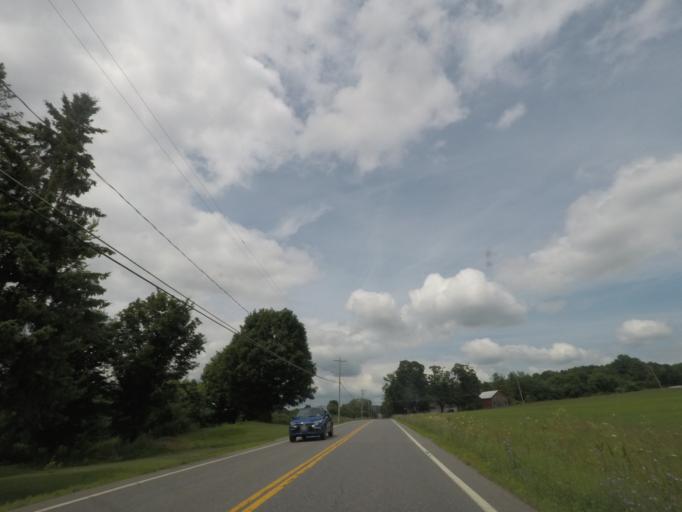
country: US
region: New York
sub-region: Saratoga County
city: Stillwater
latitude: 43.0171
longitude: -73.6920
